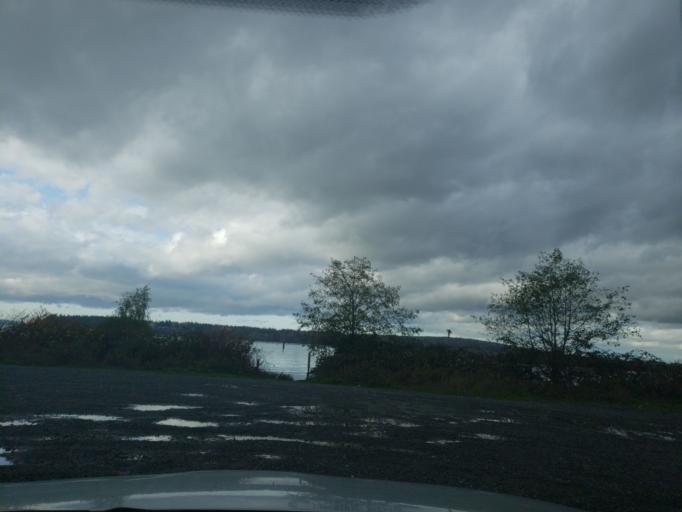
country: US
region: Washington
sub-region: Snohomish County
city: Everett
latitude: 48.0171
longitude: -122.2065
